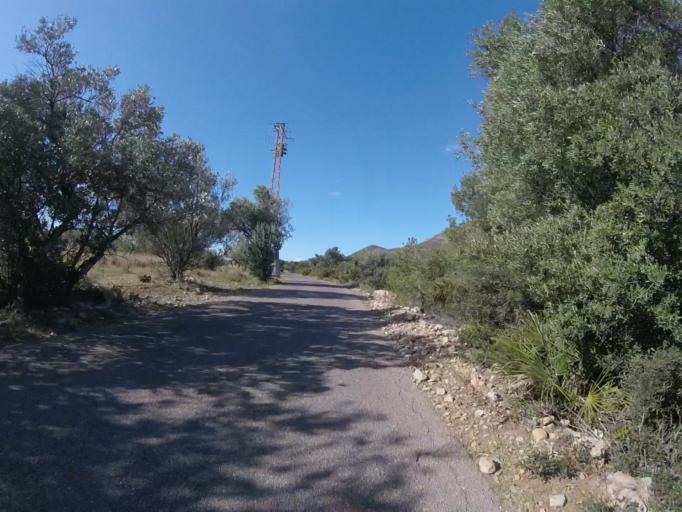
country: ES
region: Valencia
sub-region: Provincia de Castello
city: Orpesa/Oropesa del Mar
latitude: 40.0894
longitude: 0.1268
